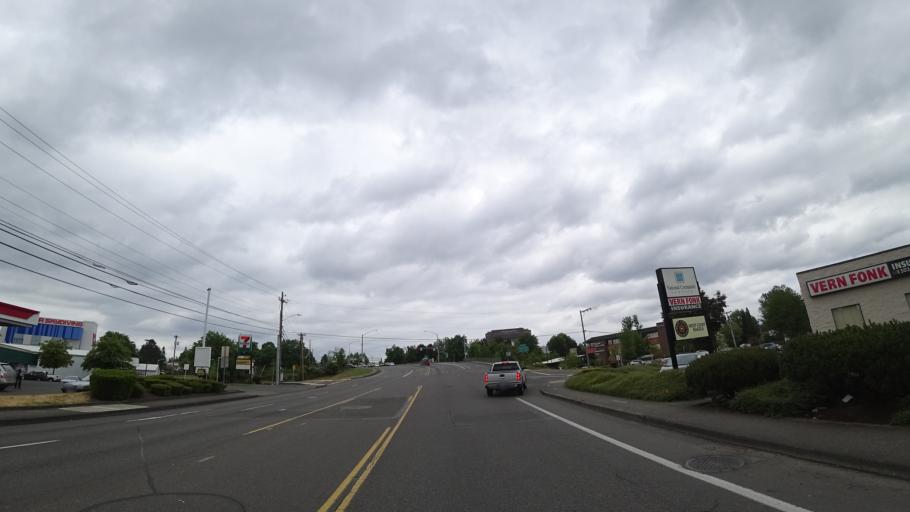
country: US
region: Oregon
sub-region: Washington County
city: Tigard
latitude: 45.4419
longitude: -122.7787
